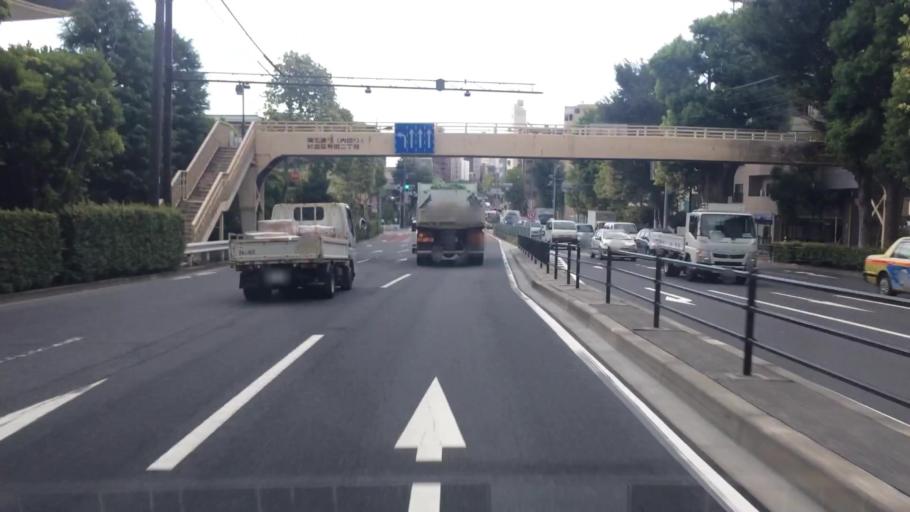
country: JP
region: Tokyo
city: Tokyo
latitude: 35.6885
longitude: 139.6553
